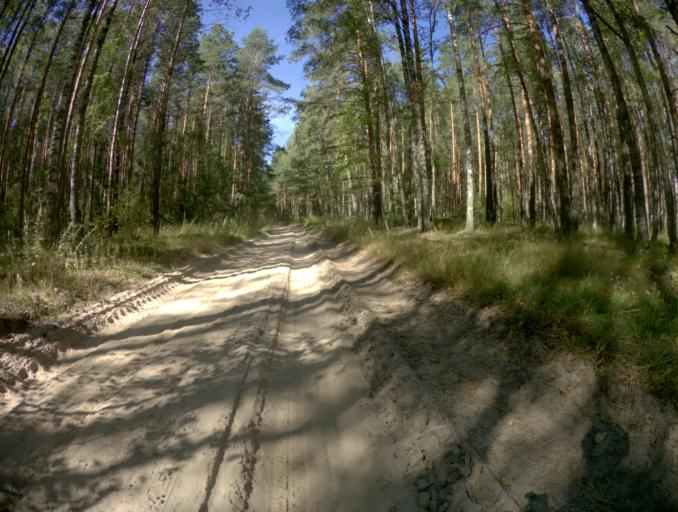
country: RU
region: Vladimir
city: Dobryatino
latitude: 55.6385
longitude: 41.3130
